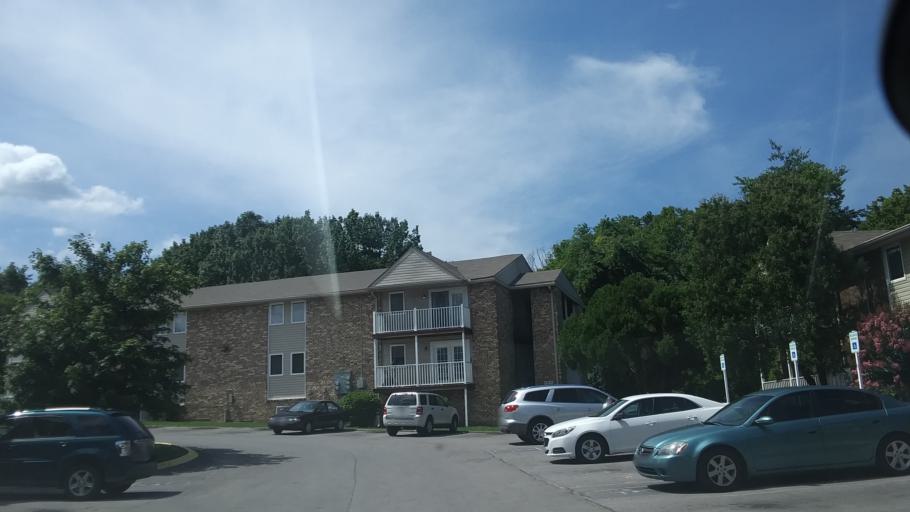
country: US
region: Tennessee
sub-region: Rutherford County
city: La Vergne
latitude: 36.0774
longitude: -86.6320
